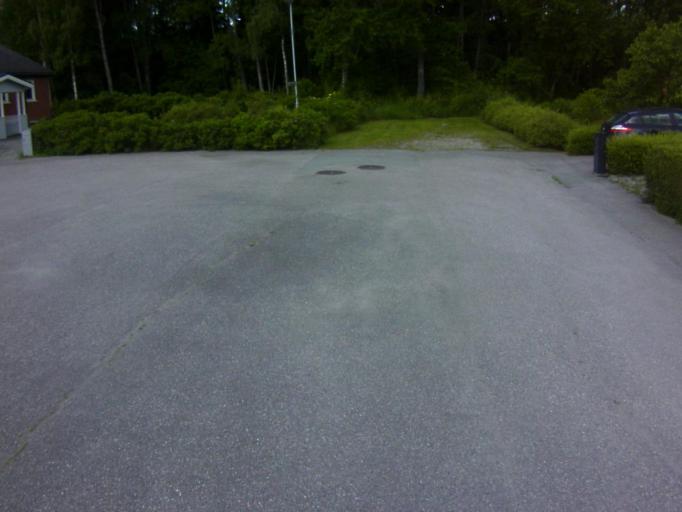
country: SE
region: Soedermanland
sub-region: Eskilstuna Kommun
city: Skogstorp
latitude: 59.3217
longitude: 16.4957
